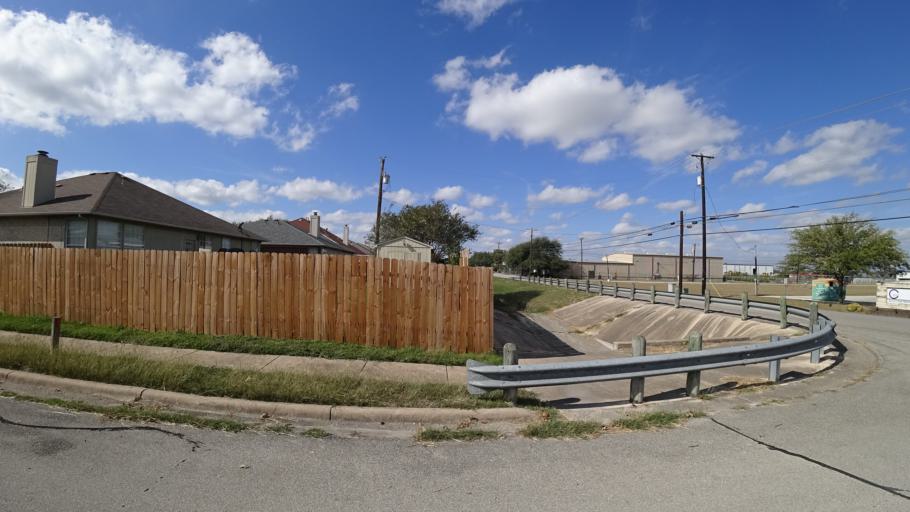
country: US
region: Texas
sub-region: Travis County
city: Windemere
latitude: 30.4588
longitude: -97.6534
